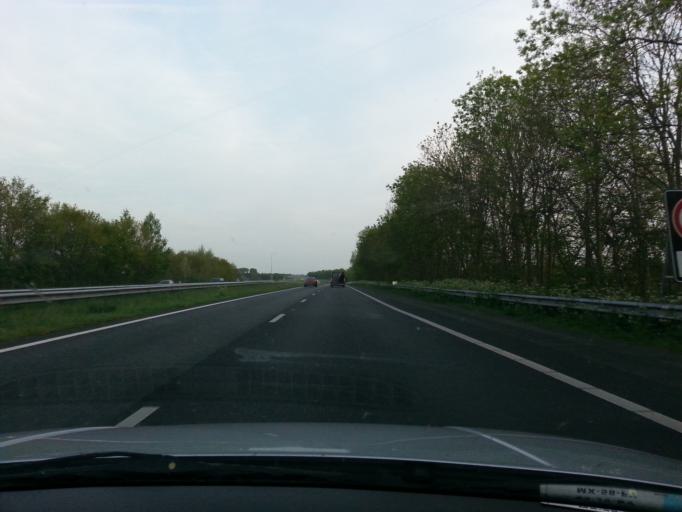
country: NL
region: Friesland
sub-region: Gemeente Lemsterland
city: Lemmer
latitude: 52.8492
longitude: 5.7215
